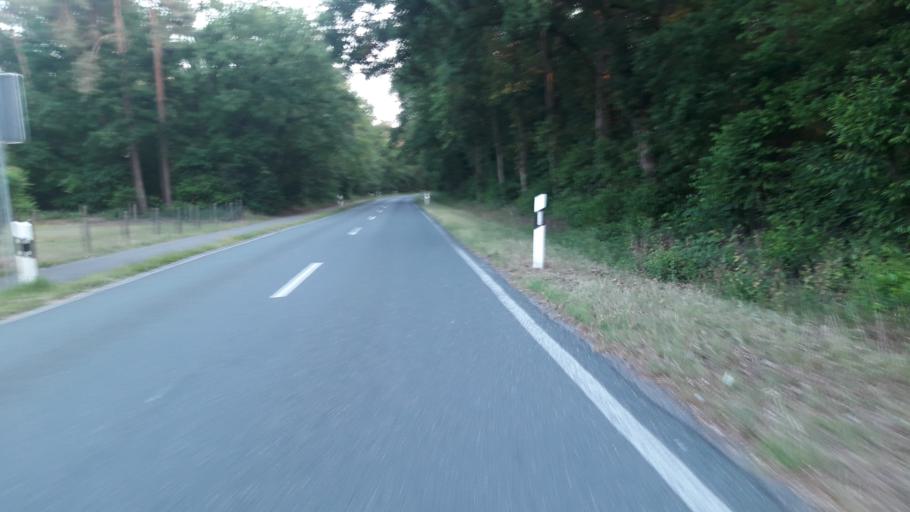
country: DE
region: North Rhine-Westphalia
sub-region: Regierungsbezirk Detmold
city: Hovelhof
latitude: 51.8691
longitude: 8.6490
